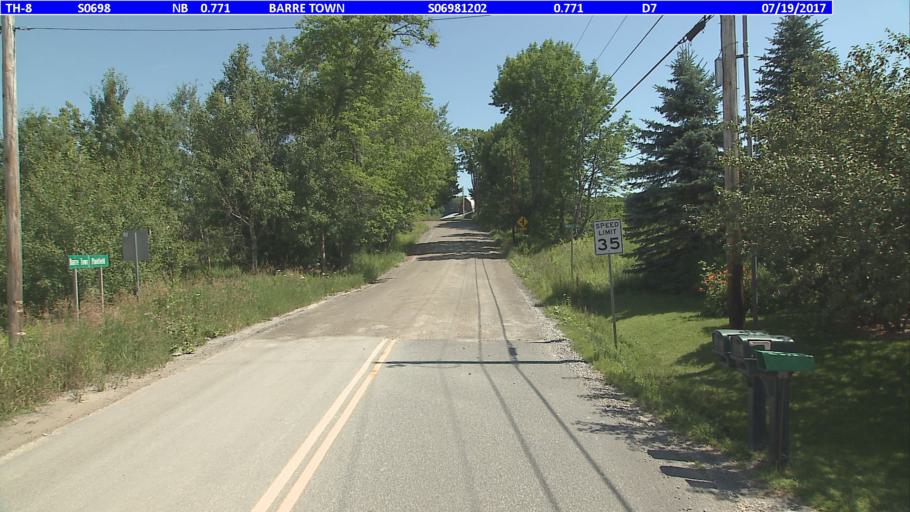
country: US
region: Vermont
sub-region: Washington County
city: Barre
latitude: 44.2293
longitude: -72.4576
